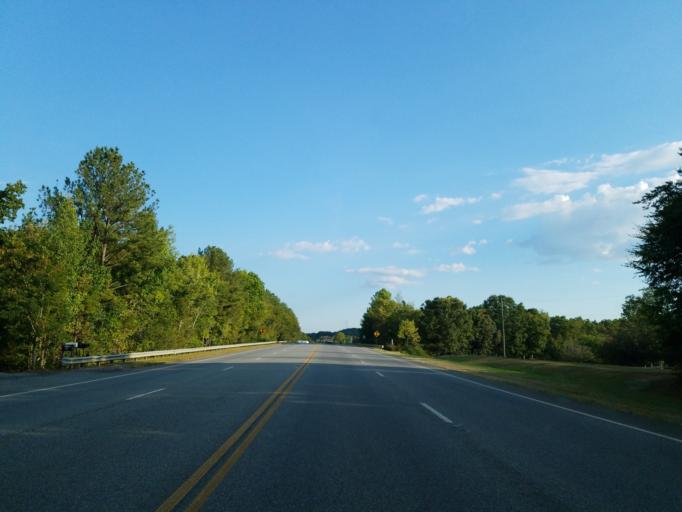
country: US
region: Georgia
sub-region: Murray County
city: Chatsworth
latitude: 34.7005
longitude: -84.7405
